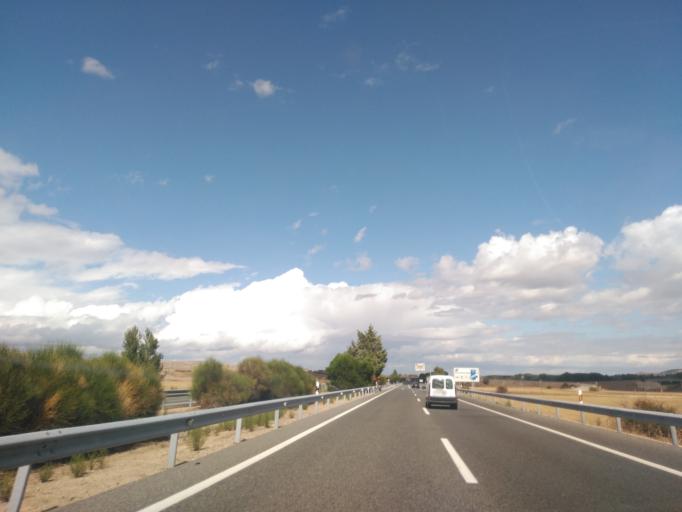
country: ES
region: Castille and Leon
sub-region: Provincia de Burgos
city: Villaldemiro
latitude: 42.2328
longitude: -3.9864
